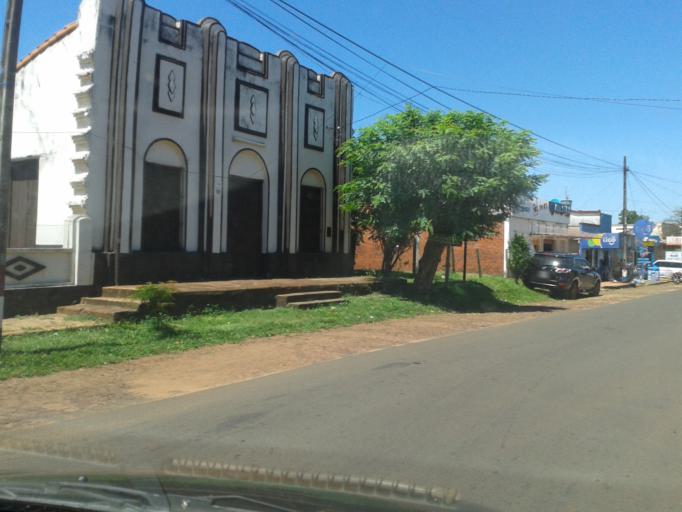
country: PY
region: Misiones
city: Santa Rosa
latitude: -26.8871
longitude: -56.8499
